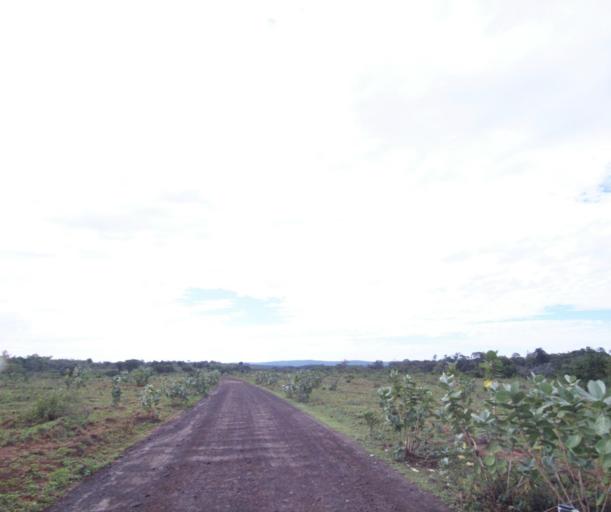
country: BR
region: Bahia
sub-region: Carinhanha
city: Carinhanha
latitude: -14.2255
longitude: -44.4372
